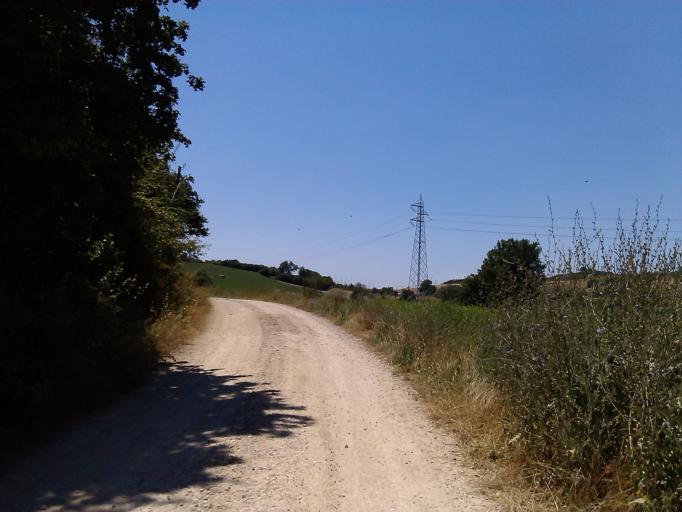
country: IT
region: Umbria
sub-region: Provincia di Terni
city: Ficulle
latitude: 42.8446
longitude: 12.0423
